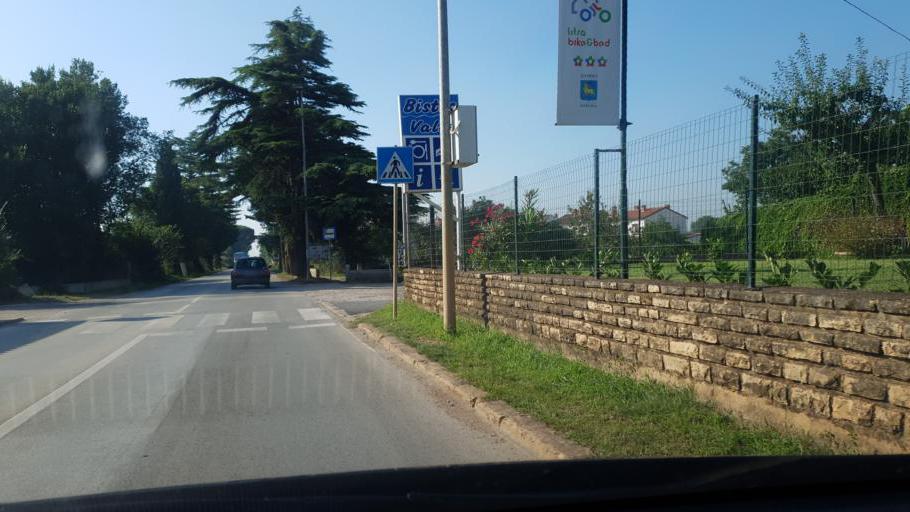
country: HR
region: Istarska
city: Fazana
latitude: 44.9101
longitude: 13.8211
